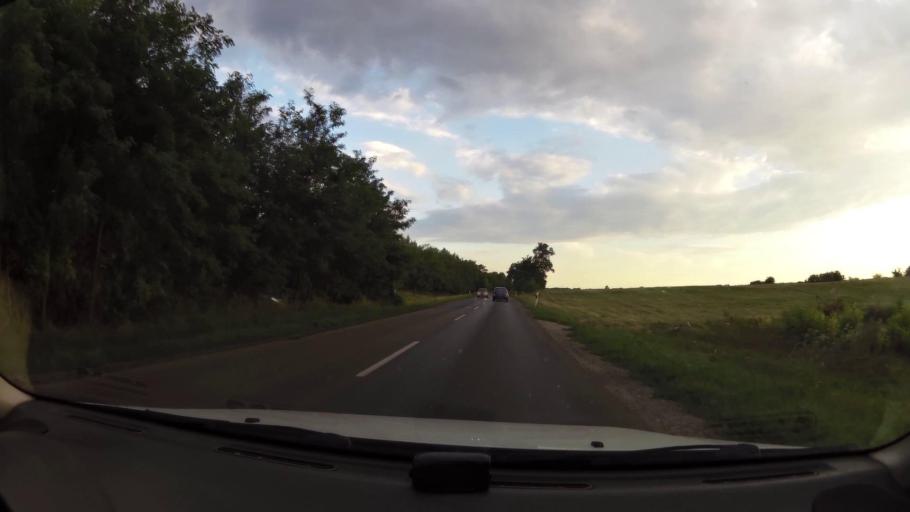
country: HU
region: Pest
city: Tapioszele
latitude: 47.3151
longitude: 19.8741
